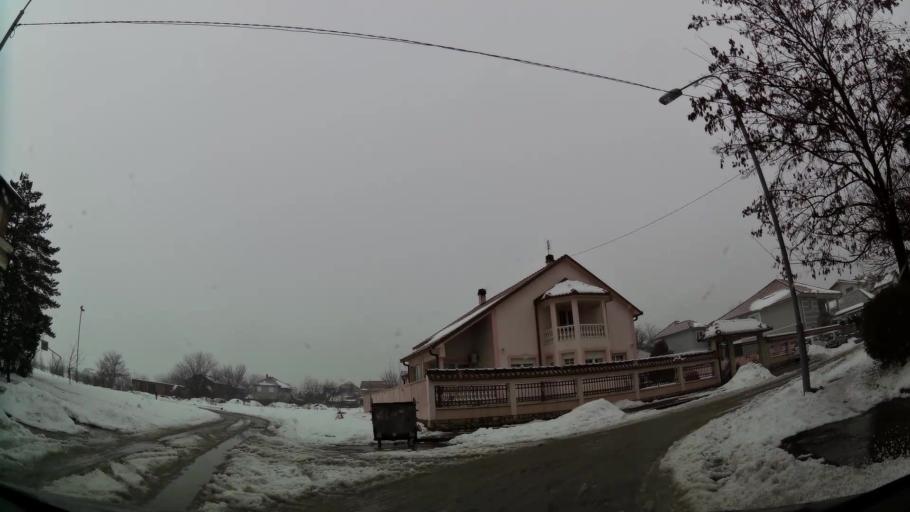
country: RS
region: Central Serbia
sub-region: Belgrade
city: Zemun
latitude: 44.8714
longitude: 20.3194
